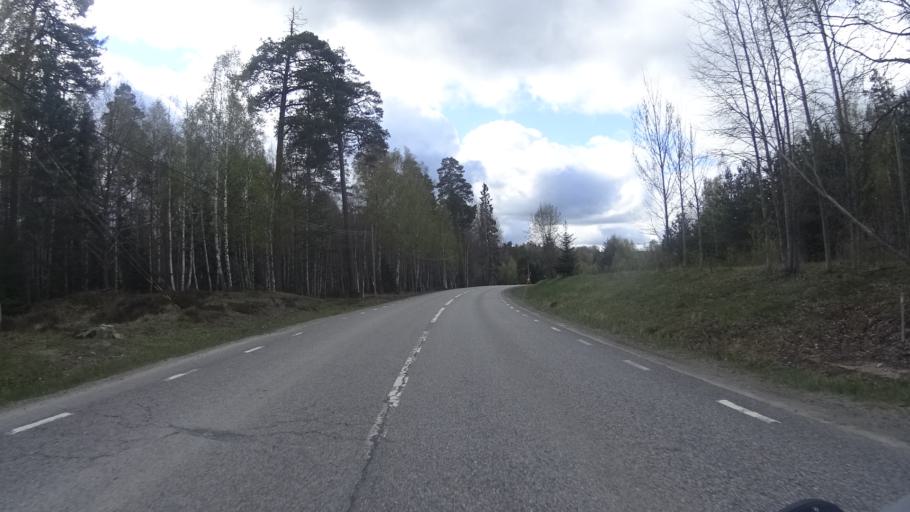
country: SE
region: Stockholm
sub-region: Botkyrka Kommun
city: Tullinge
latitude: 59.1766
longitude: 17.9292
